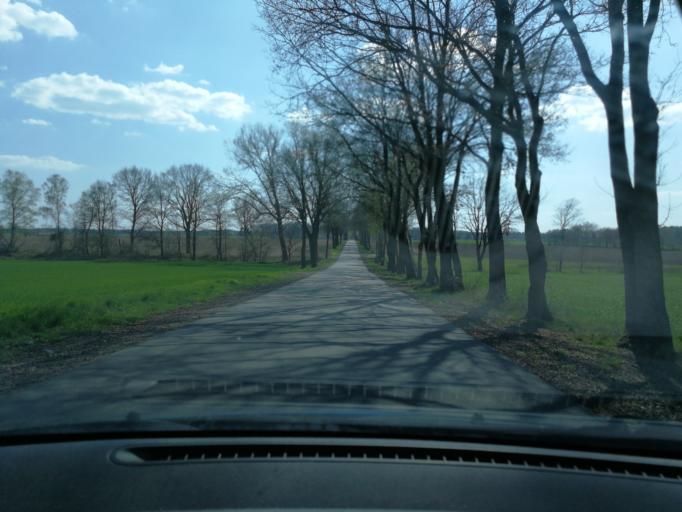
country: DE
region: Lower Saxony
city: Reinstorf
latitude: 53.2113
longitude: 10.5862
